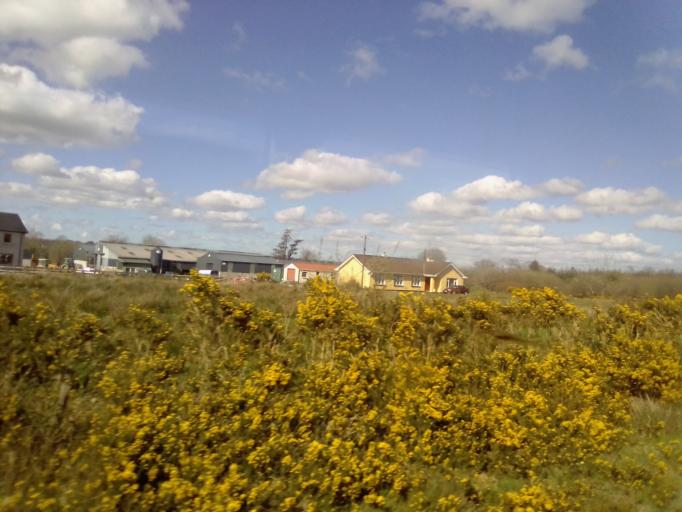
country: IE
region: Munster
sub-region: County Cork
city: Millstreet
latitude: 52.0860
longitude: -9.0153
